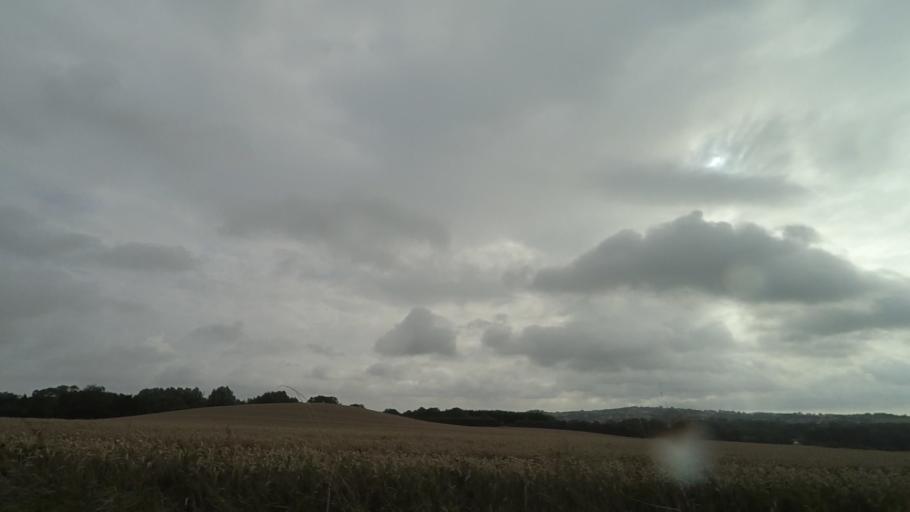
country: DK
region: Central Jutland
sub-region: Syddjurs Kommune
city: Ronde
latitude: 56.3031
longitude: 10.4432
